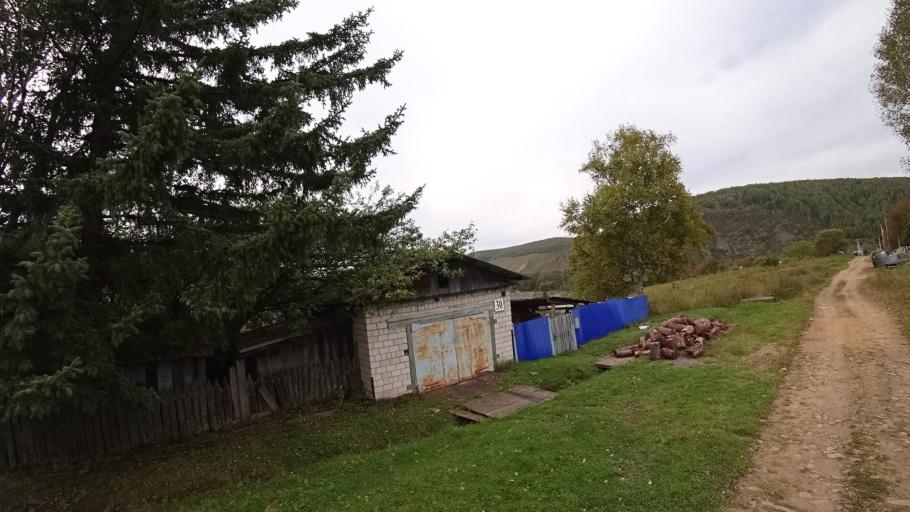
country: RU
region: Jewish Autonomous Oblast
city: Khingansk
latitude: 49.1277
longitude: 131.2035
